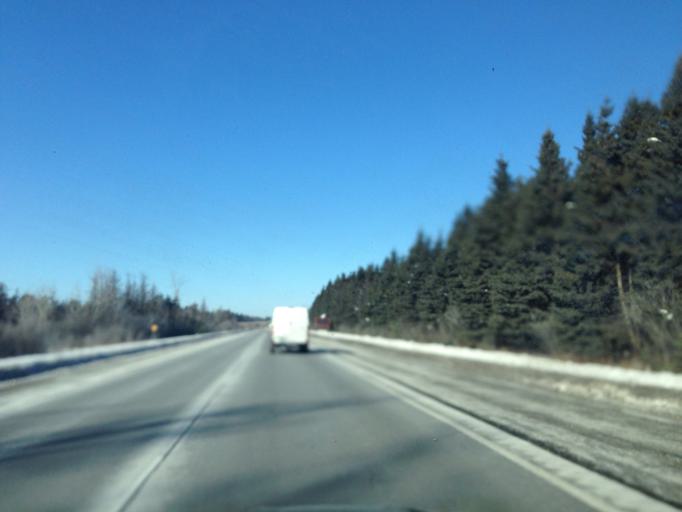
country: CA
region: Ontario
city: Ottawa
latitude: 45.3652
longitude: -75.5102
